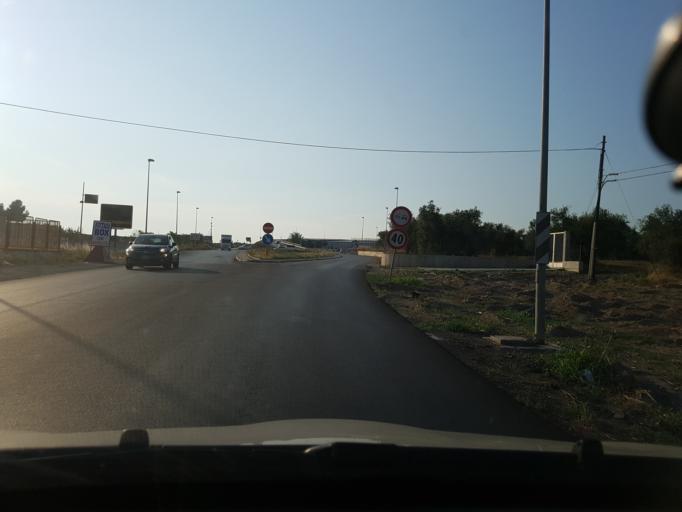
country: IT
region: Apulia
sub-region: Provincia di Foggia
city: Cerignola
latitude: 41.2724
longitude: 15.8773
